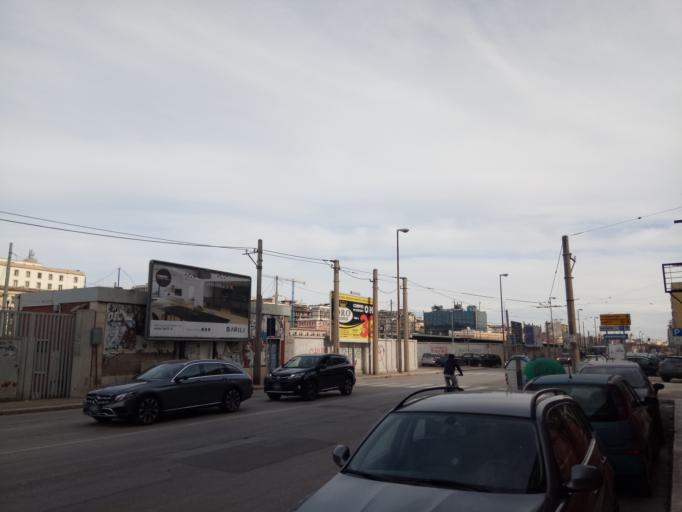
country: IT
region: Apulia
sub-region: Provincia di Bari
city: Bari
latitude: 41.1166
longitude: 16.8659
